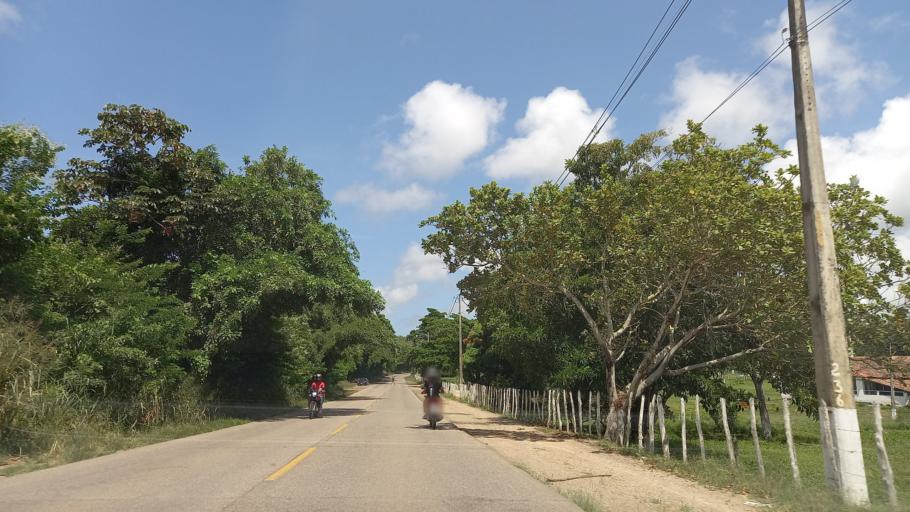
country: BR
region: Pernambuco
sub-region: Sirinhaem
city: Sirinhaem
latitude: -8.6382
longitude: -35.1187
